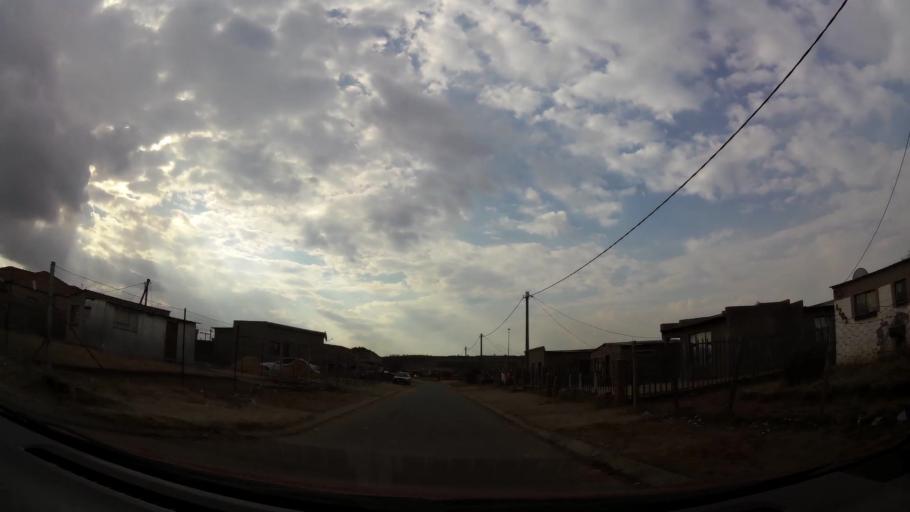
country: ZA
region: Gauteng
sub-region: Sedibeng District Municipality
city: Vanderbijlpark
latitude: -26.6763
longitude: 27.8586
